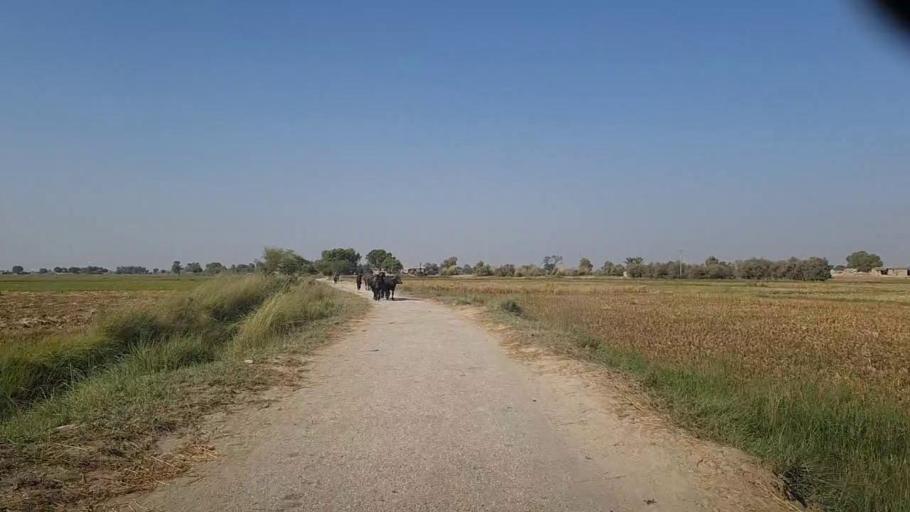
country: PK
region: Sindh
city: Tangwani
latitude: 28.2564
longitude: 68.9376
